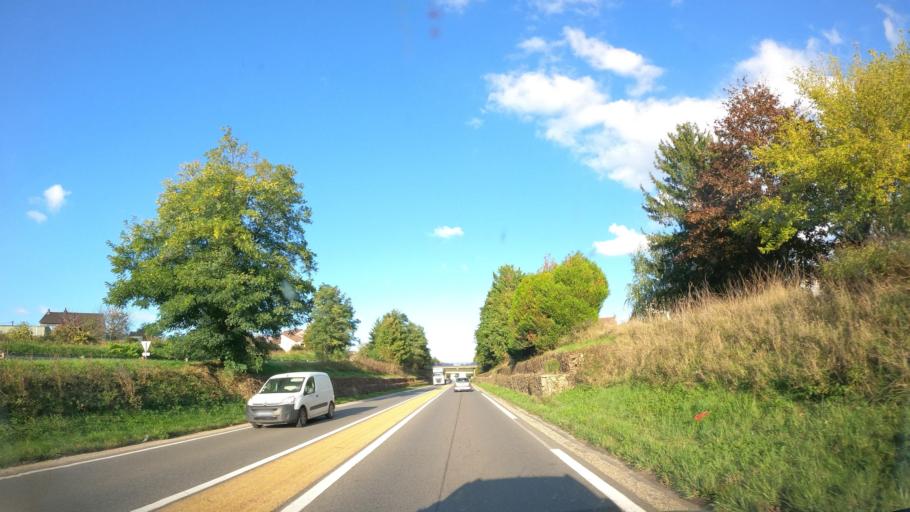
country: FR
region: Bourgogne
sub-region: Departement de Saone-et-Loire
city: Blanzy
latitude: 46.6988
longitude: 4.3884
